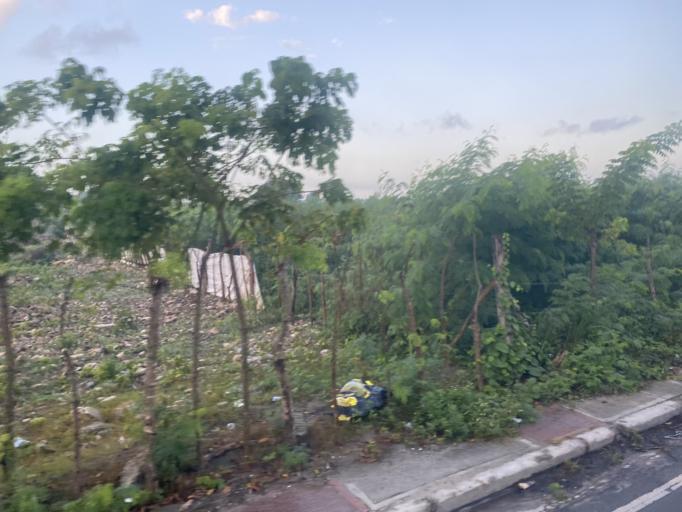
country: DO
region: San Juan
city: Punta Cana
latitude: 18.7104
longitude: -68.4633
